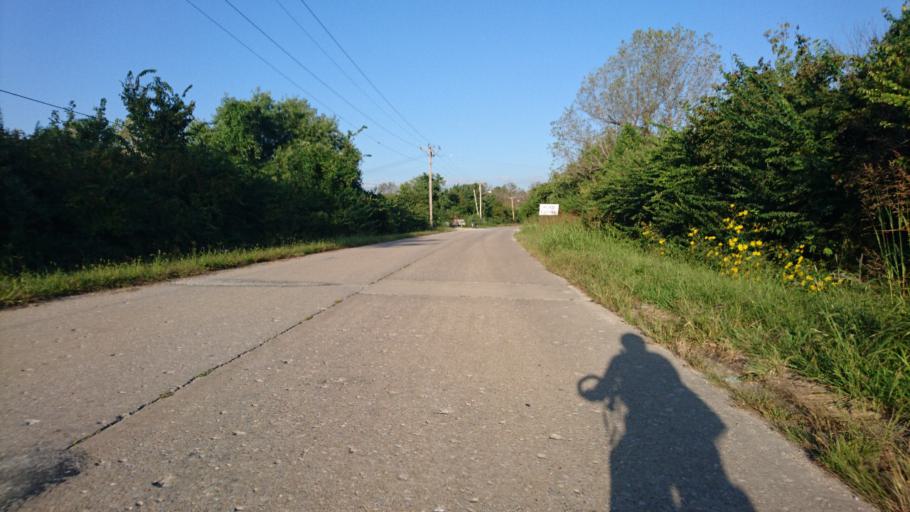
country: US
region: Missouri
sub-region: Saint Louis County
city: Glasgow Village
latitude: 38.7564
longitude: -90.1607
